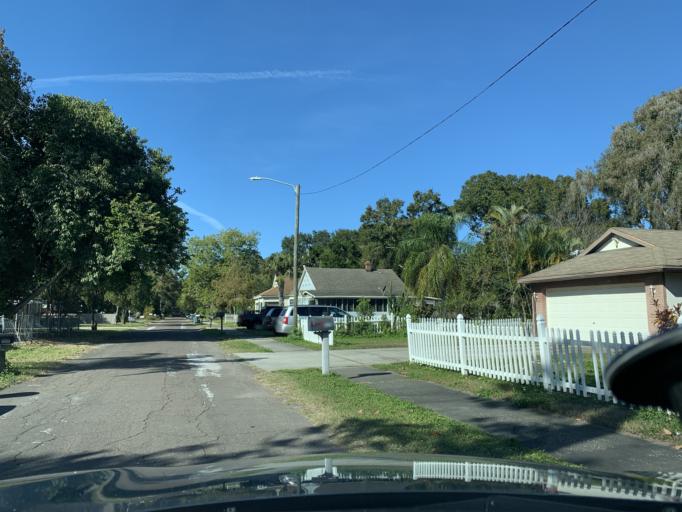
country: US
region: Florida
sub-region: Pinellas County
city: Gulfport
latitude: 27.7550
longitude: -82.7019
